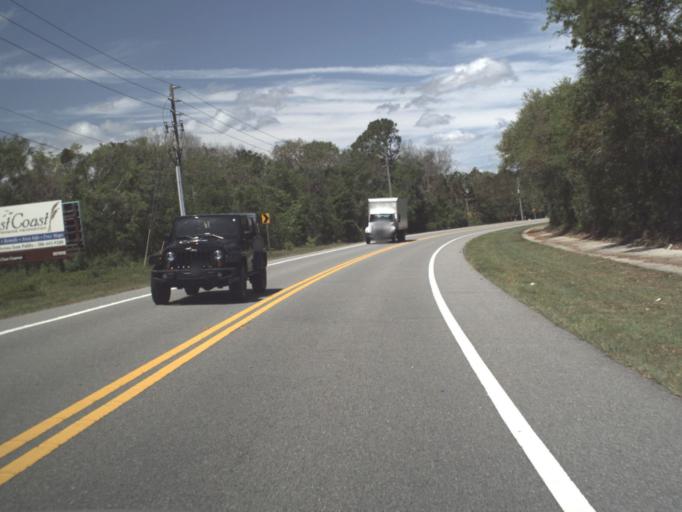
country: US
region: Florida
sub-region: Flagler County
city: Palm Coast
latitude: 29.5638
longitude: -81.1793
